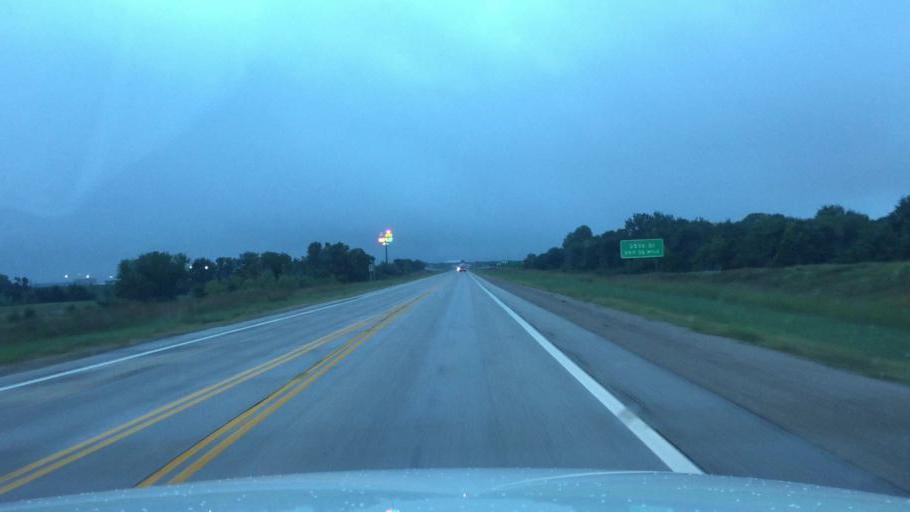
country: US
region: Kansas
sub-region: Neosho County
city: Chanute
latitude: 37.6557
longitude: -95.4797
